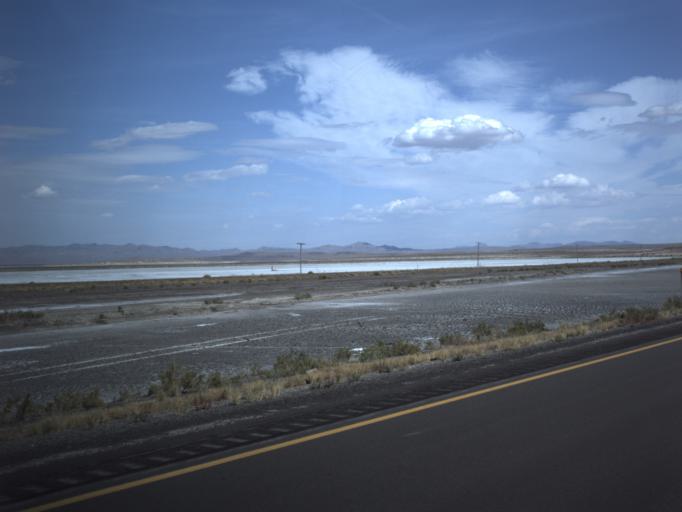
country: US
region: Utah
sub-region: Tooele County
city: Wendover
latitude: 40.7266
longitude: -113.2716
